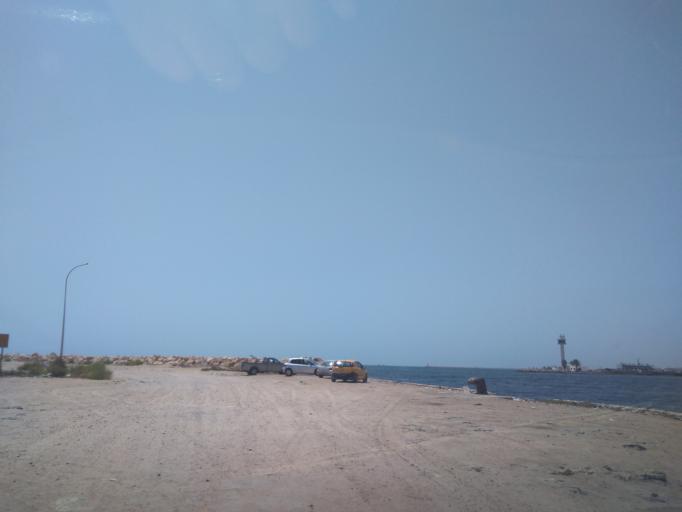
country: TN
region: Safaqis
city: Sfax
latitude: 34.7244
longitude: 10.7791
